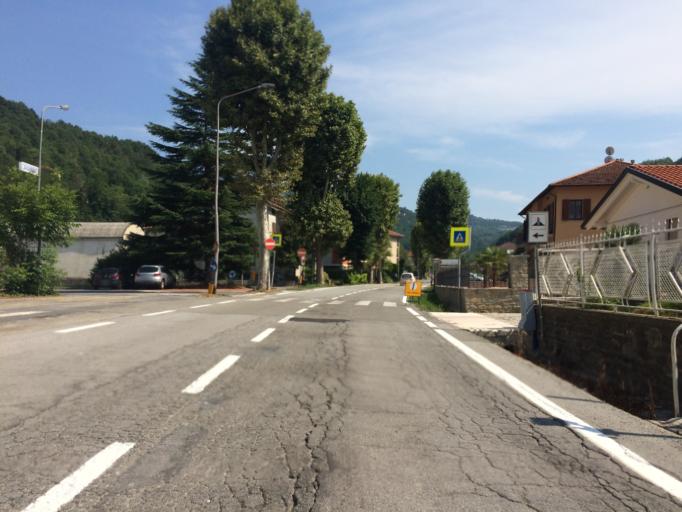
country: IT
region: Piedmont
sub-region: Provincia di Cuneo
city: Cortemilia
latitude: 44.5750
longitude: 8.1992
